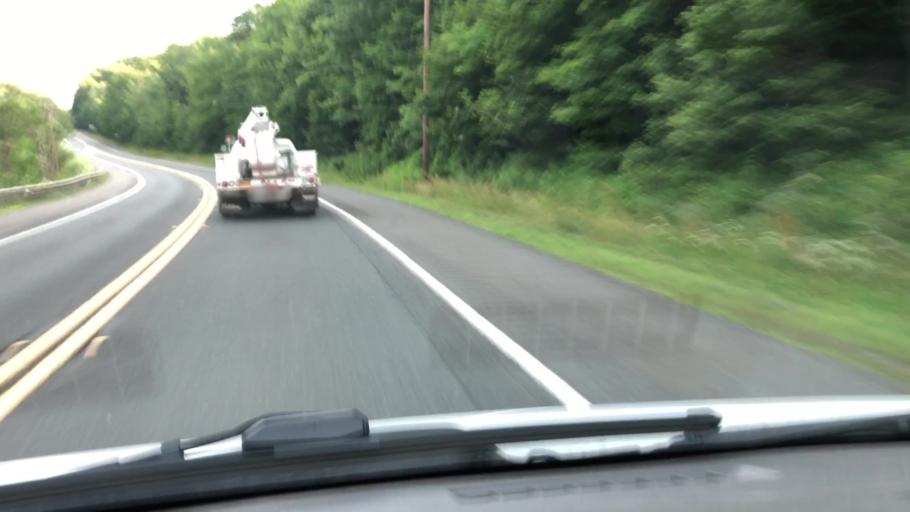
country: US
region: Massachusetts
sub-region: Hampshire County
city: Chesterfield
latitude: 42.4518
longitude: -72.8761
